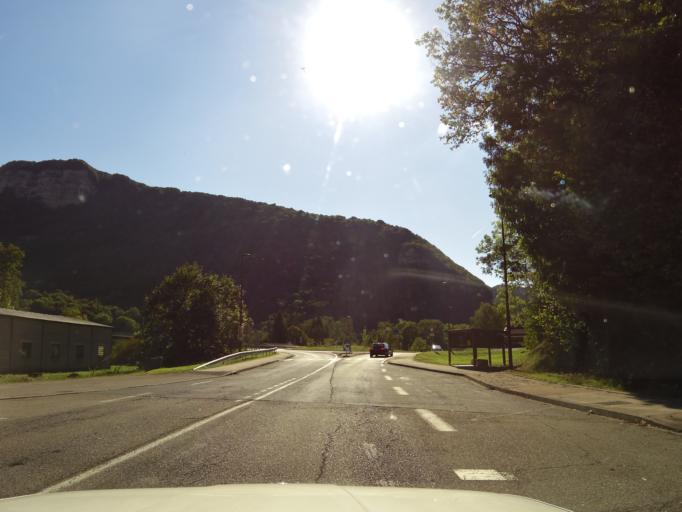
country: FR
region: Rhone-Alpes
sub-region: Departement de l'Ain
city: Saint-Rambert-en-Bugey
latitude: 45.9364
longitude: 5.4258
